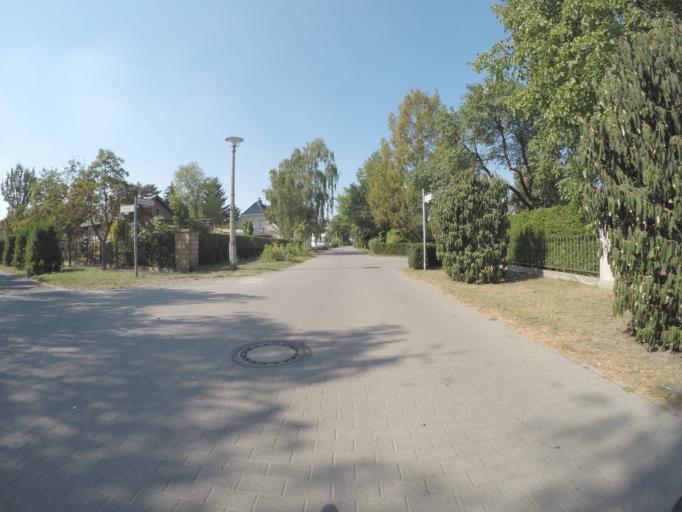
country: DE
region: Berlin
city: Kopenick Bezirk
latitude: 52.4754
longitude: 13.5636
